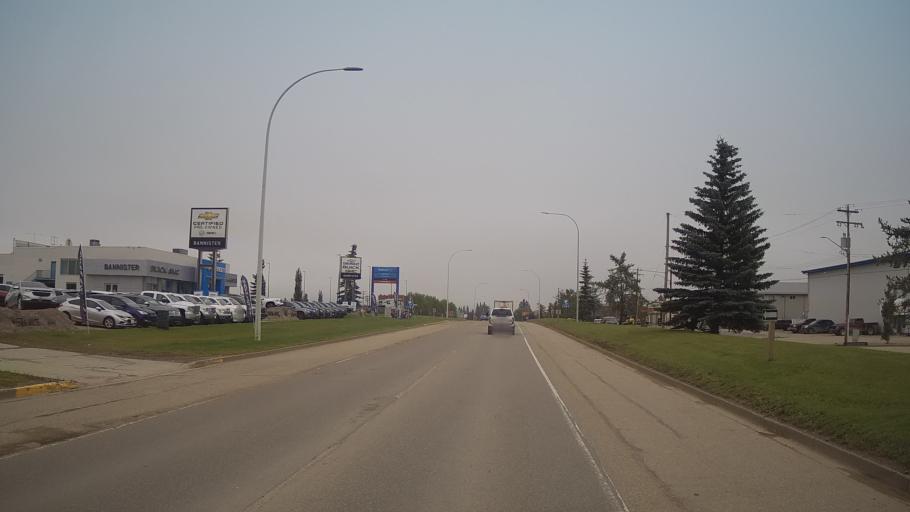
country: CA
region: Alberta
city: Edson
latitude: 53.5752
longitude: -116.4531
